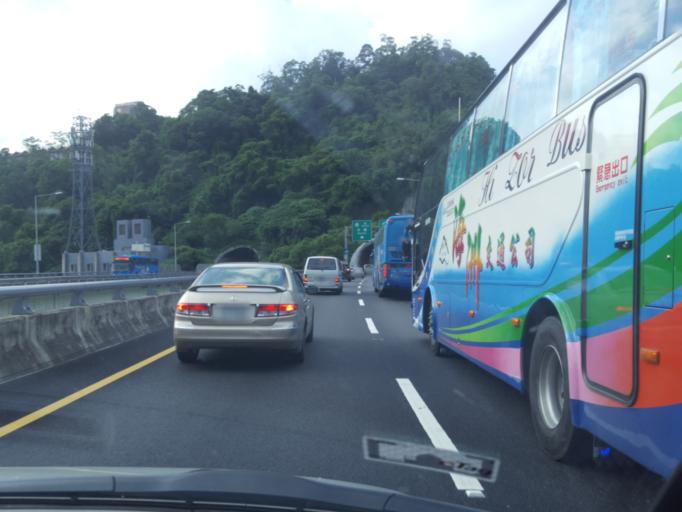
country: TW
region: Taipei
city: Taipei
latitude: 25.0115
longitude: 121.6450
